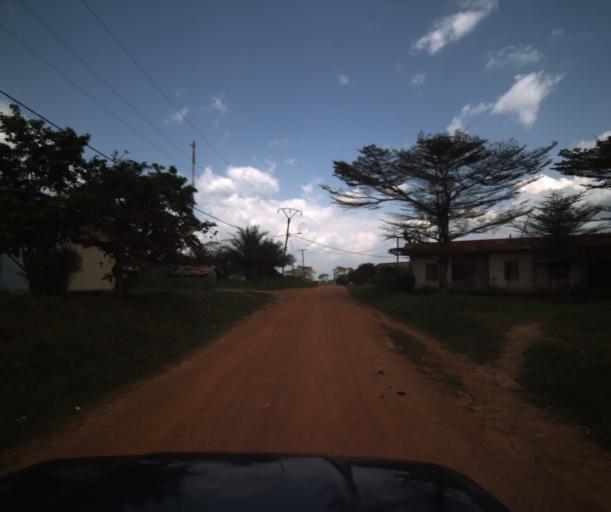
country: CM
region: Centre
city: Eseka
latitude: 3.5466
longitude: 11.0306
